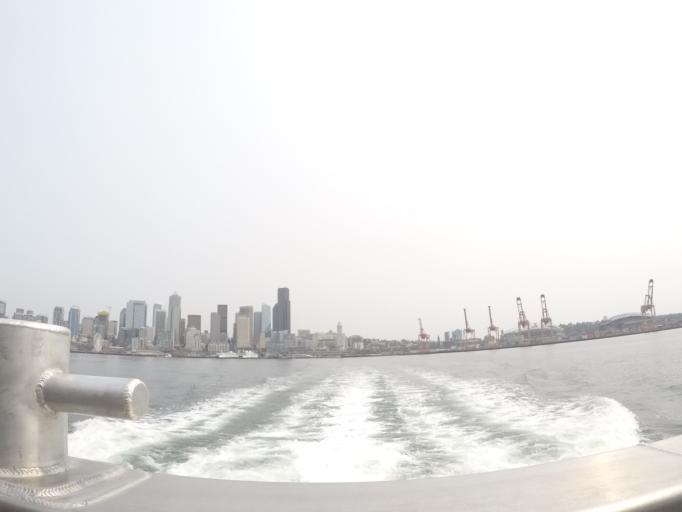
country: US
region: Washington
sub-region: King County
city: Seattle
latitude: 47.5977
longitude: -122.3532
